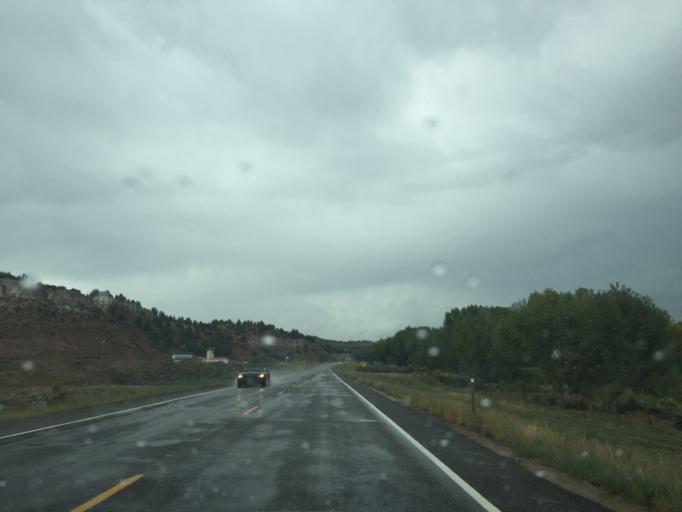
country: US
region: Utah
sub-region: Kane County
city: Kanab
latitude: 37.2338
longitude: -112.6752
